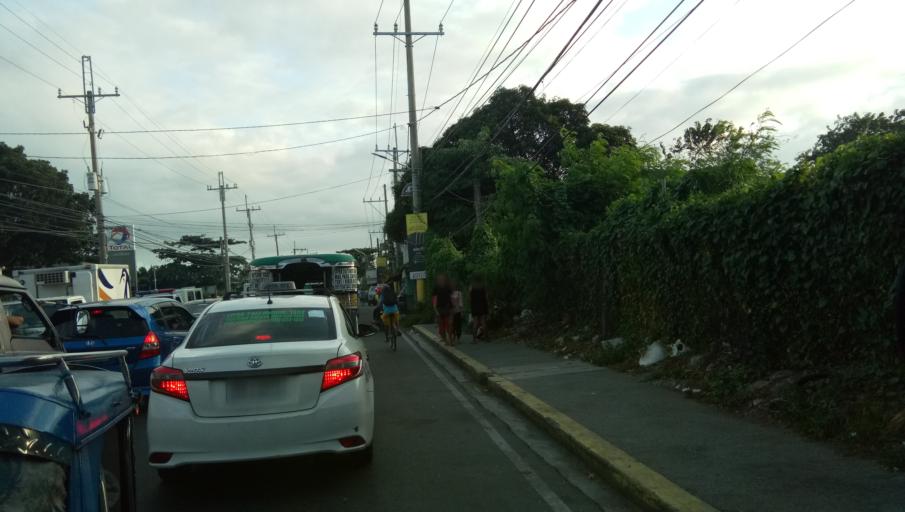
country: PH
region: Calabarzon
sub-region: Province of Cavite
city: Imus
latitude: 14.3820
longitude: 120.9784
